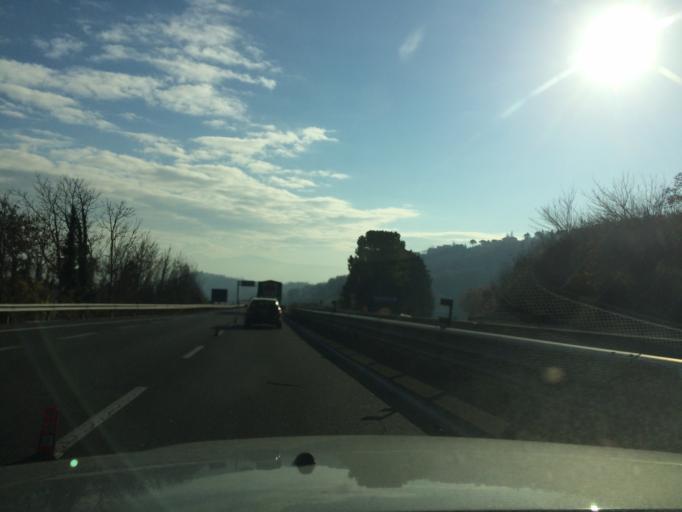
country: IT
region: Umbria
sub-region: Provincia di Terni
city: San Gemini
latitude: 42.6180
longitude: 12.5537
